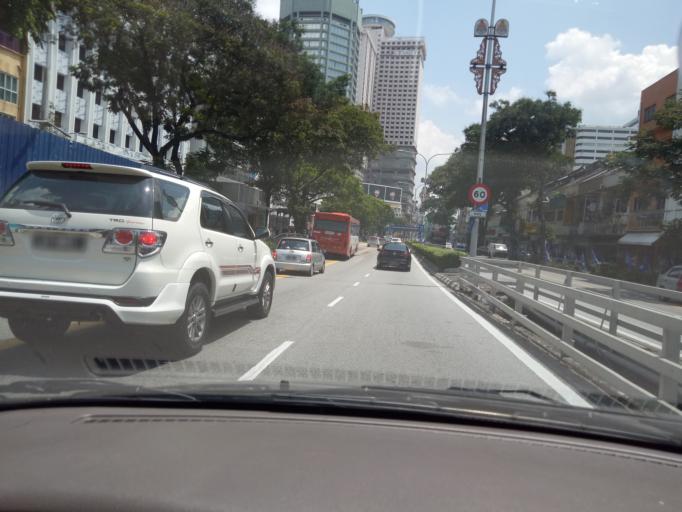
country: MY
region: Kuala Lumpur
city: Kuala Lumpur
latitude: 3.1700
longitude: 101.6948
